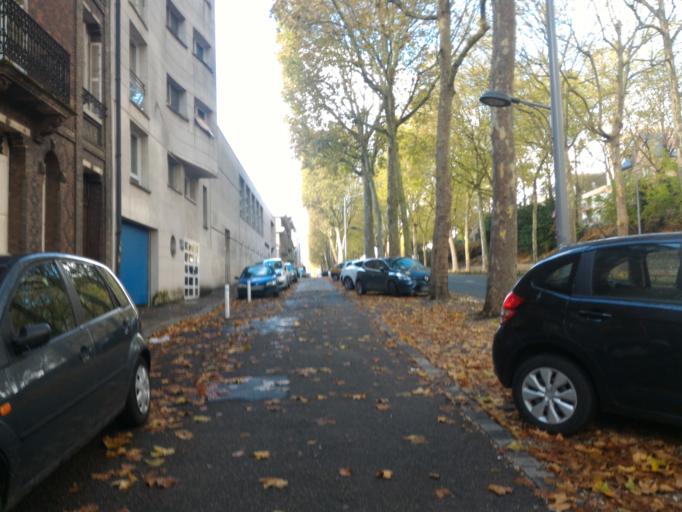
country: FR
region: Haute-Normandie
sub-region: Departement de la Seine-Maritime
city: Rouen
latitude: 49.4446
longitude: 1.1114
